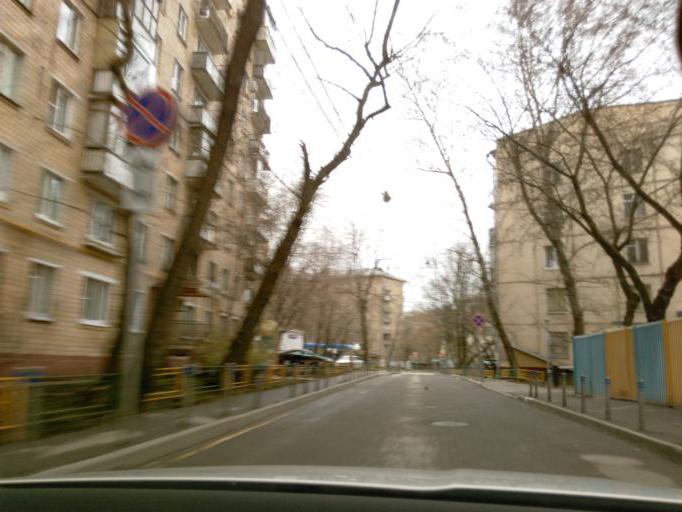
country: RU
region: Moskovskaya
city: Dorogomilovo
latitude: 55.7672
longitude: 37.5863
